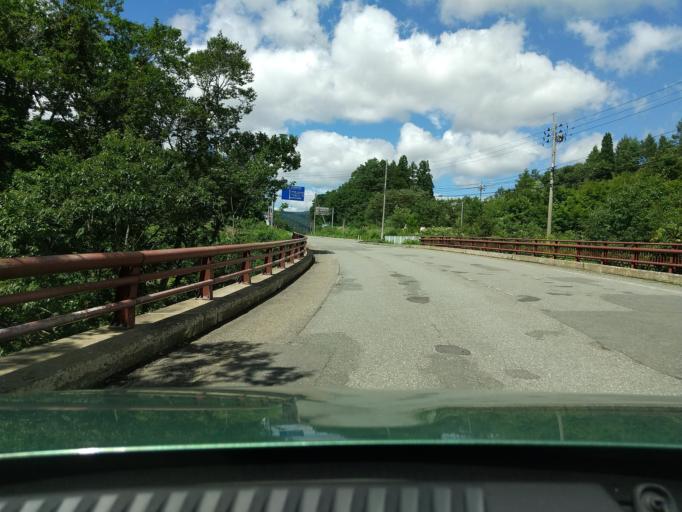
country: JP
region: Iwate
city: Shizukuishi
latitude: 39.7690
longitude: 140.7640
